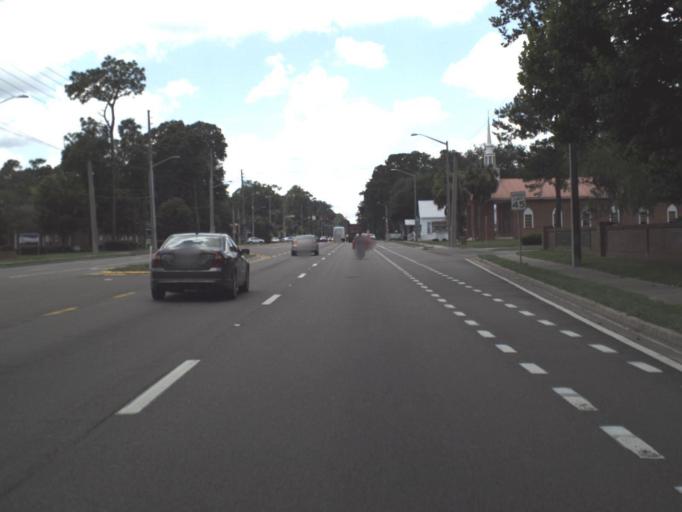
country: US
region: Florida
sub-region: Alachua County
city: Gainesville
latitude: 29.6888
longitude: -82.3863
